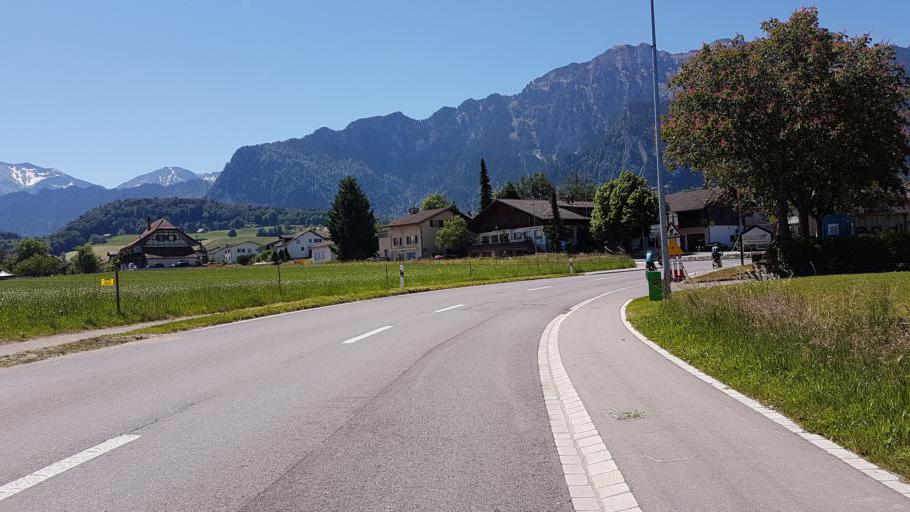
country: CH
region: Bern
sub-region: Thun District
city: Thierachern
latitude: 46.7287
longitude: 7.5845
